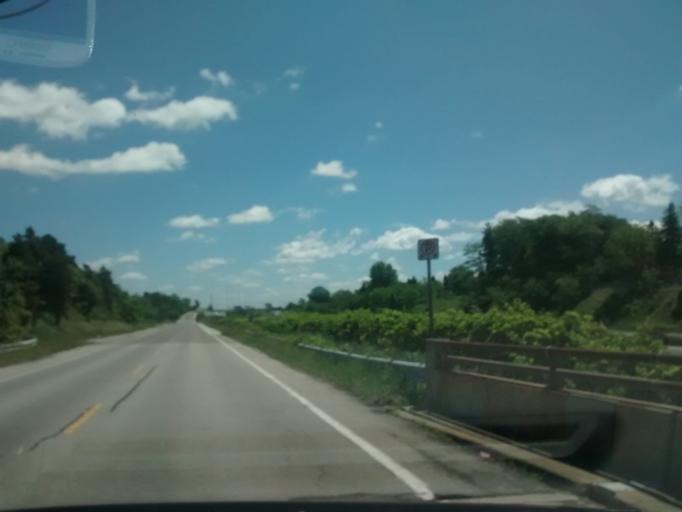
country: CA
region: Ontario
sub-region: Regional Municipality of Niagara
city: St. Catharines
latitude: 43.1803
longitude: -79.3265
